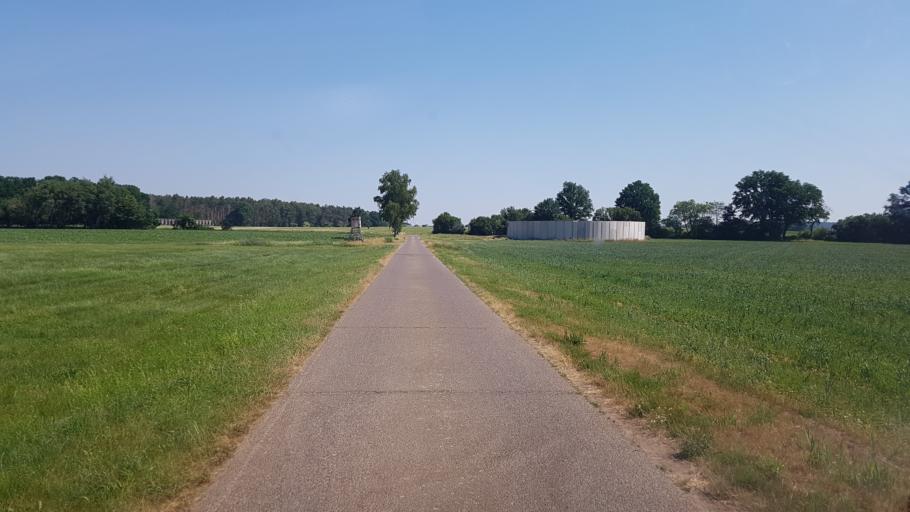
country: DE
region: Brandenburg
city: Lebusa
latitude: 51.8028
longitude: 13.4331
